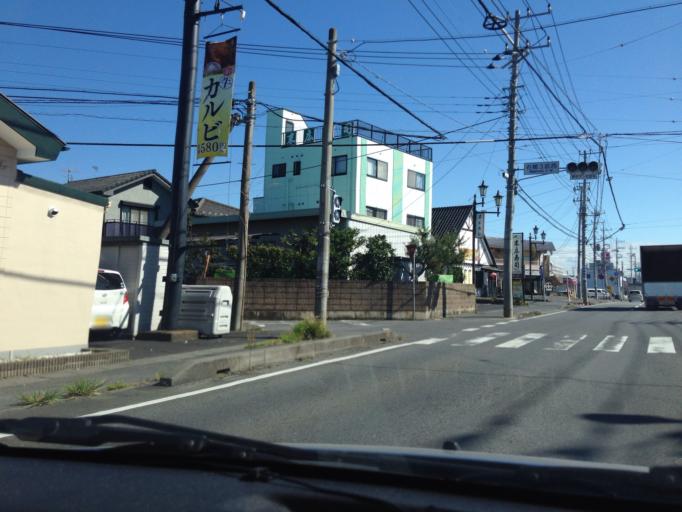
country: JP
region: Ibaraki
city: Naka
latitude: 36.0361
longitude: 140.1799
